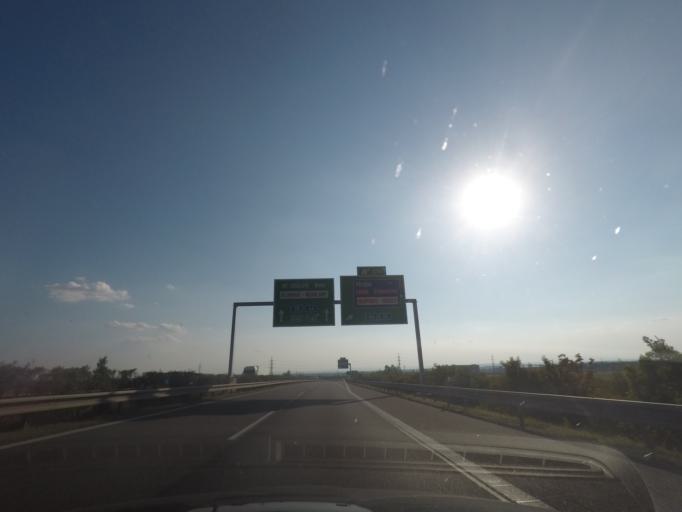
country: CZ
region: Olomoucky
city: Velky Tynec
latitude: 49.5629
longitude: 17.3259
